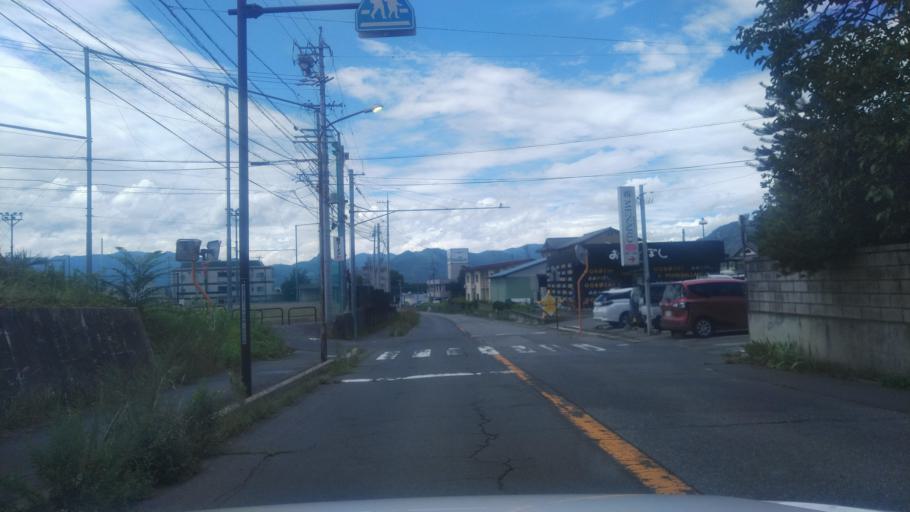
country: JP
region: Nagano
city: Ueda
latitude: 36.4021
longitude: 138.2719
